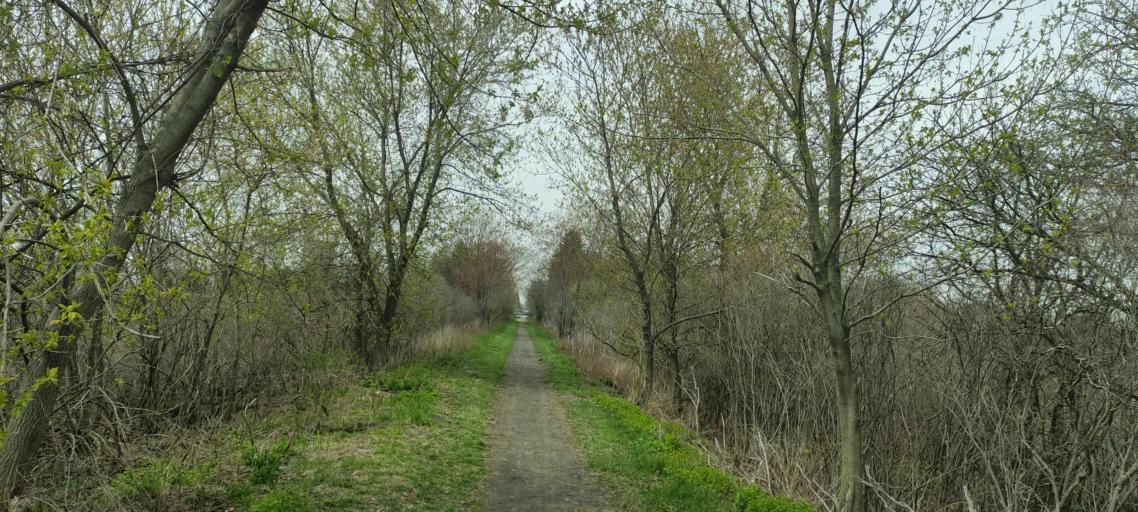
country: CA
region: Ontario
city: Stratford
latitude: 43.3188
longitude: -80.8273
